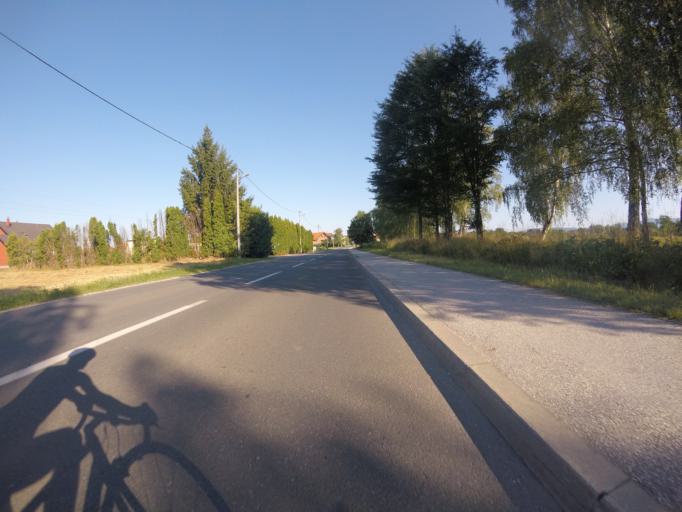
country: HR
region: Grad Zagreb
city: Zadvorsko
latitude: 45.7285
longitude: 15.9056
